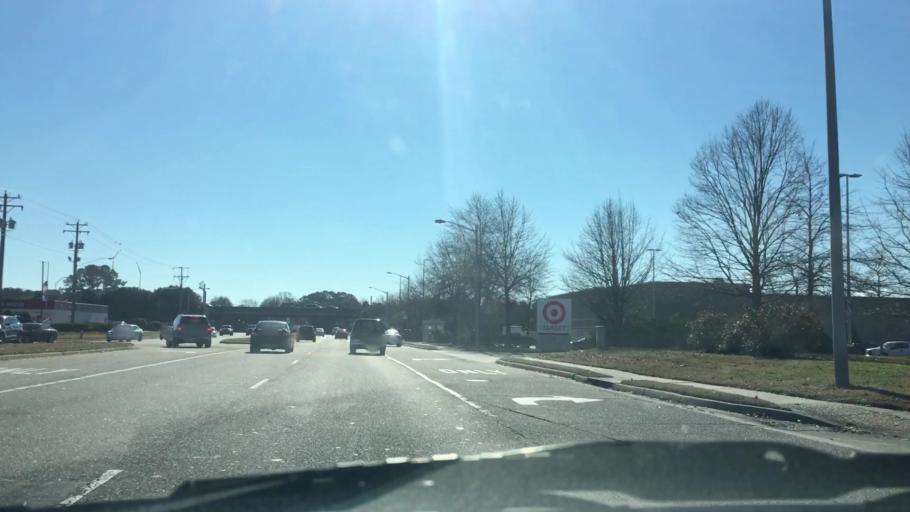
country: US
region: Virginia
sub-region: City of Virginia Beach
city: Virginia Beach
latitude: 36.8478
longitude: -76.0215
